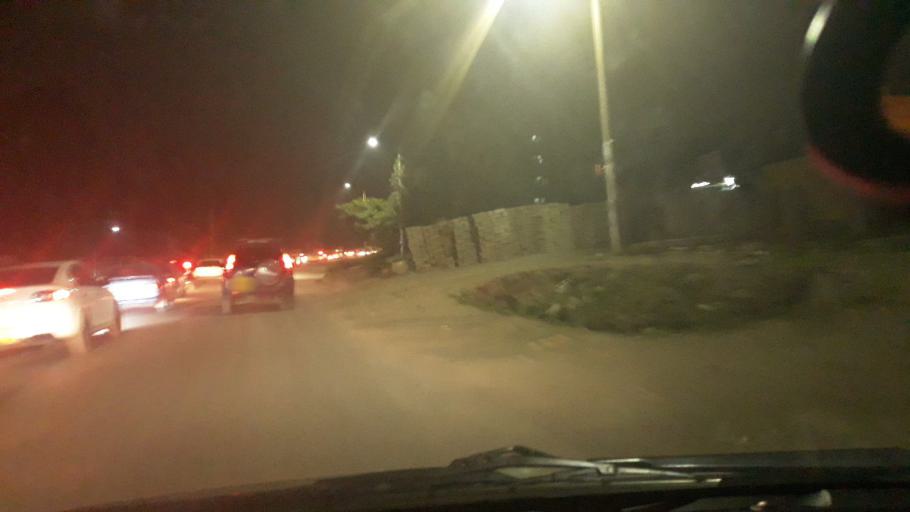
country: KE
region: Nairobi Area
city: Pumwani
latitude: -1.2772
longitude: 36.8852
